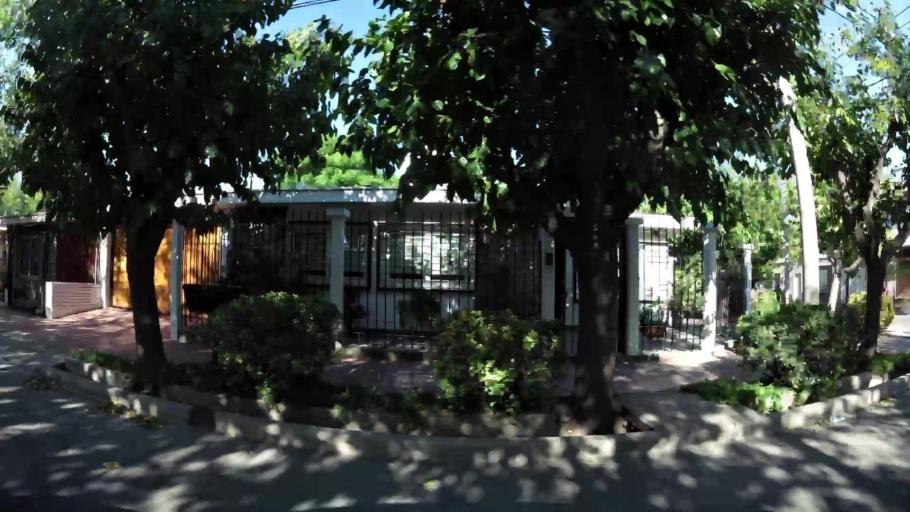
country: AR
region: Mendoza
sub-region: Departamento de Godoy Cruz
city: Godoy Cruz
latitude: -32.9128
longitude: -68.8246
